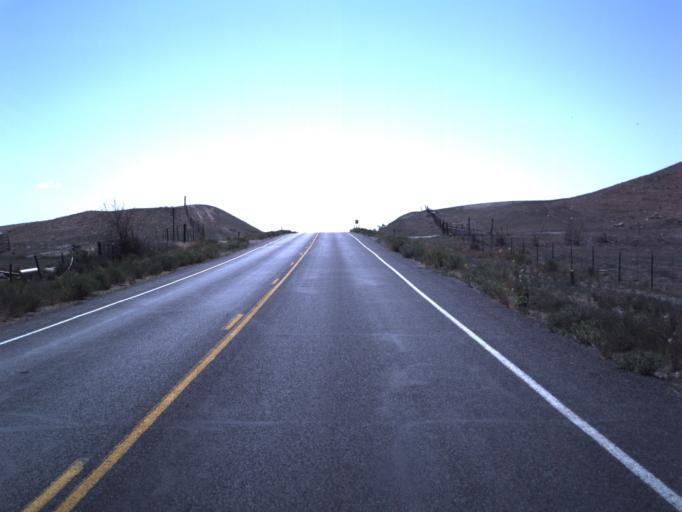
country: US
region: Utah
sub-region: Emery County
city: Castle Dale
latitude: 39.1855
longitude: -111.0477
